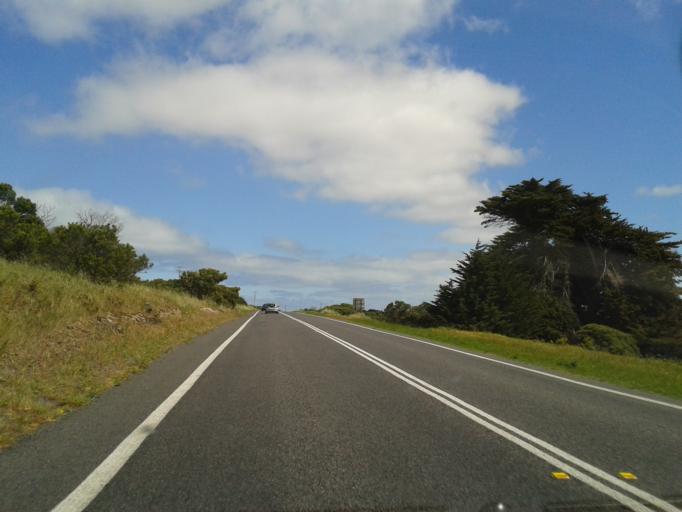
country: AU
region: Victoria
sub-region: Moyne
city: Port Fairy
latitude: -38.3494
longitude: 142.1200
